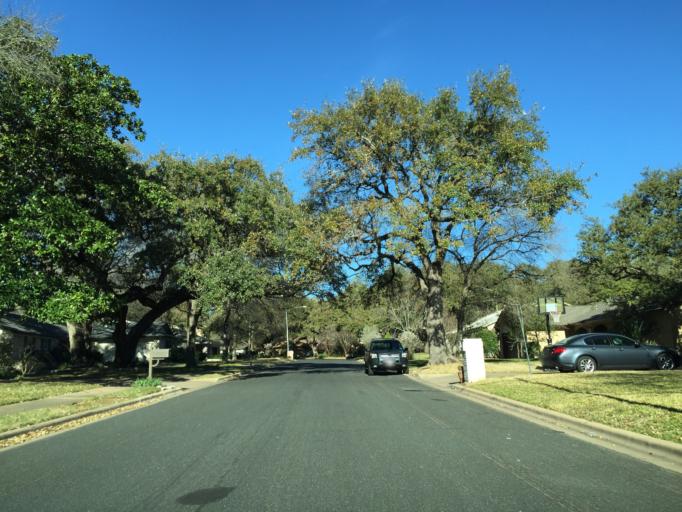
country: US
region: Texas
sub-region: Williamson County
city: Jollyville
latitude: 30.4032
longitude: -97.7339
